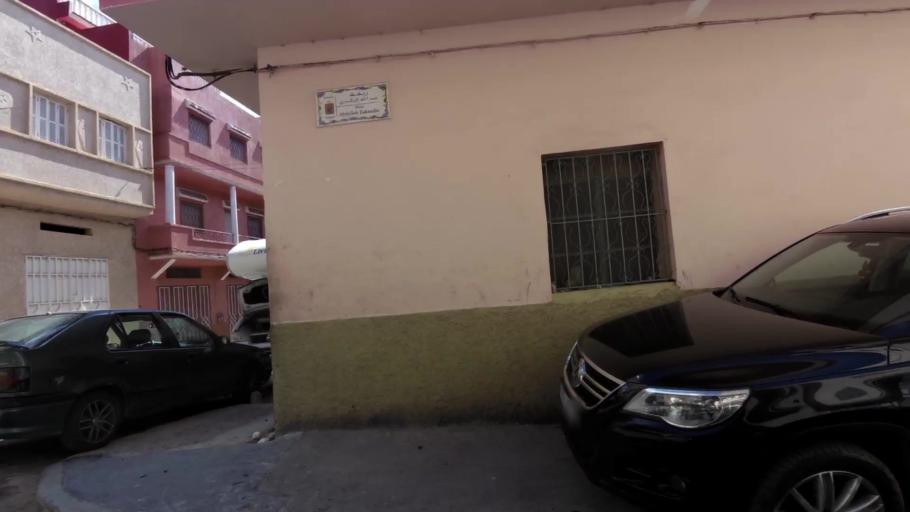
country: MA
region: Tanger-Tetouan
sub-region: Tanger-Assilah
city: Tangier
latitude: 35.7717
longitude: -5.8283
